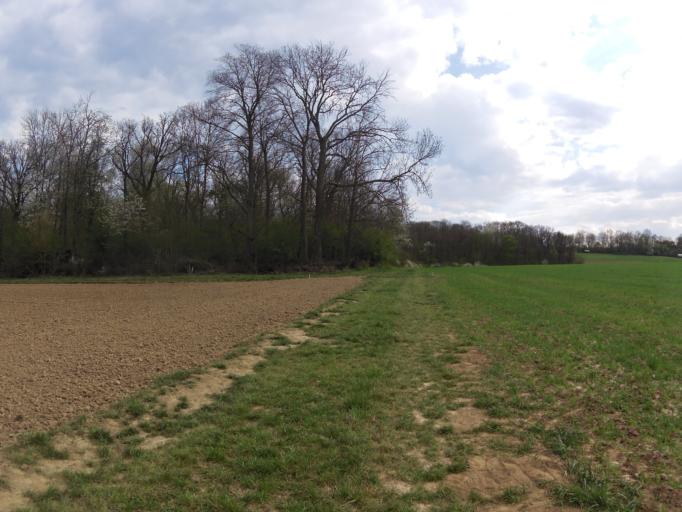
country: DE
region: Bavaria
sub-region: Regierungsbezirk Unterfranken
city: Kurnach
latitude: 49.8431
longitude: 10.0621
